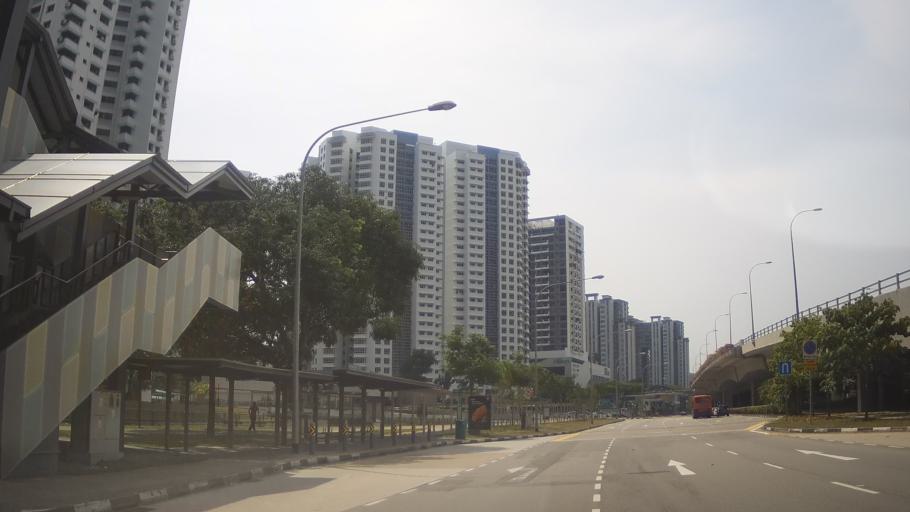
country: MY
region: Johor
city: Johor Bahru
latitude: 1.3804
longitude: 103.7601
